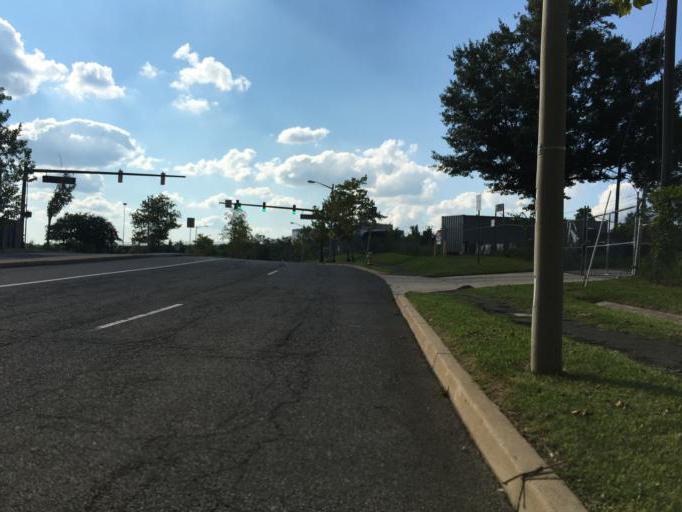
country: US
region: Virginia
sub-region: Fairfax County
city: Huntington
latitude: 38.8033
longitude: -77.0693
